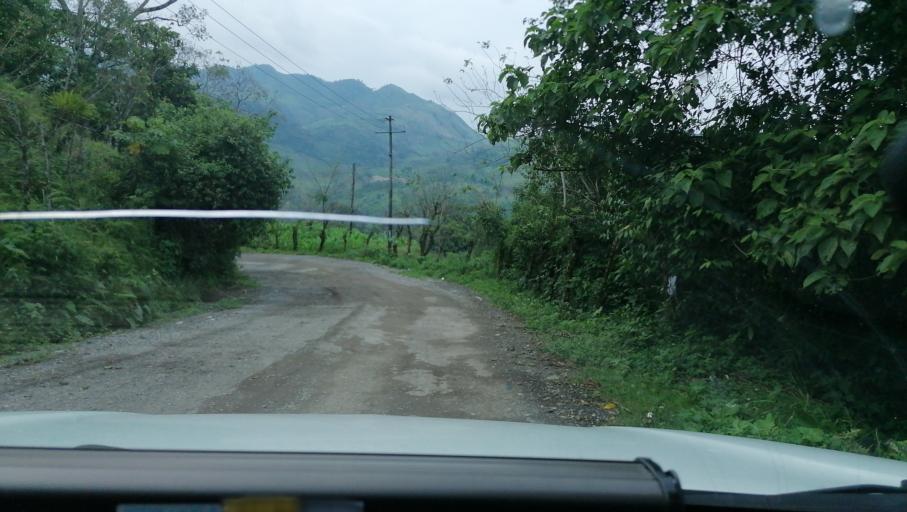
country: MX
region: Chiapas
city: Ixtacomitan
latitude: 17.3484
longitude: -93.1314
